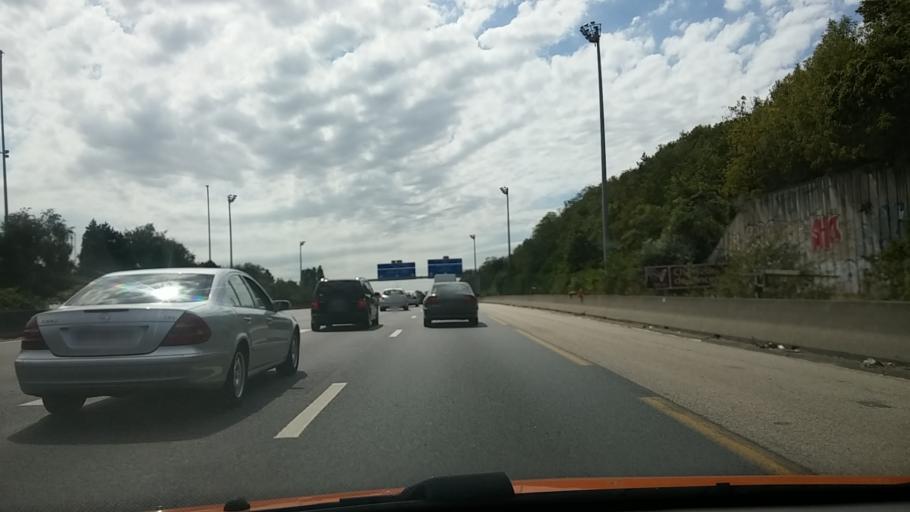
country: FR
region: Ile-de-France
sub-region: Departement du Val-de-Marne
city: Joinville-le-Pont
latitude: 48.8202
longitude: 2.4599
